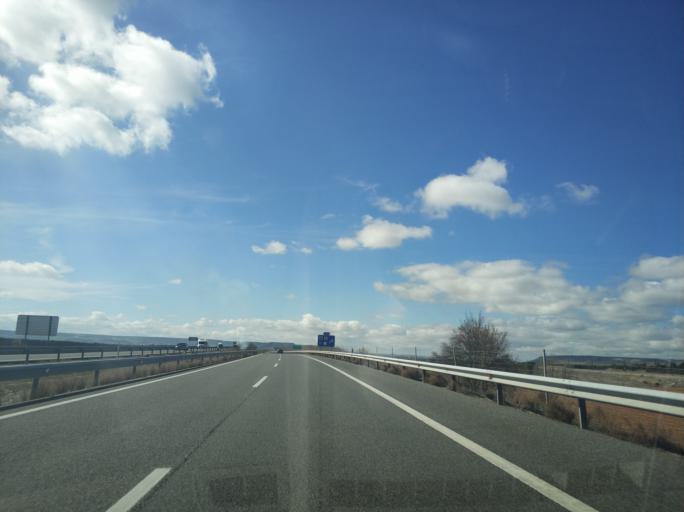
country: ES
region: Castille and Leon
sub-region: Provincia de Burgos
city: Villaverde-Mogina
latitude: 42.1675
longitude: -4.0730
